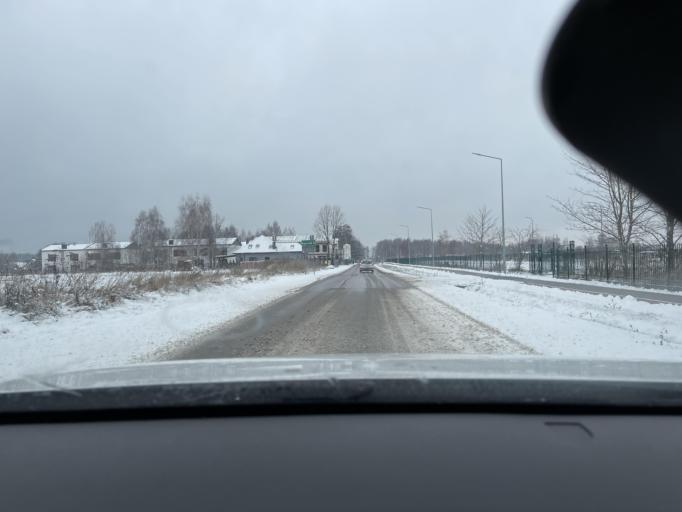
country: PL
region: Masovian Voivodeship
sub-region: Powiat zyrardowski
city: Zyrardow
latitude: 52.0348
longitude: 20.4533
